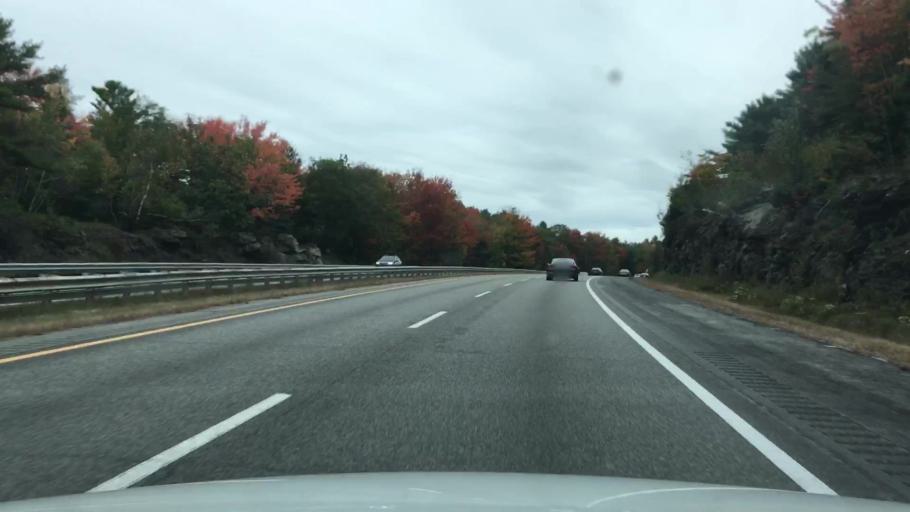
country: US
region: Maine
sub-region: Cumberland County
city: Freeport
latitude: 43.9003
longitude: -70.0749
